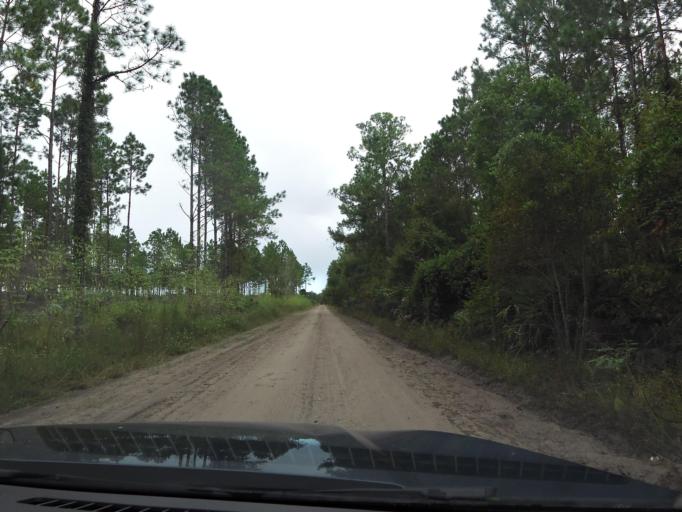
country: US
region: Florida
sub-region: Flagler County
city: Palm Coast
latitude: 29.5931
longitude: -81.3522
